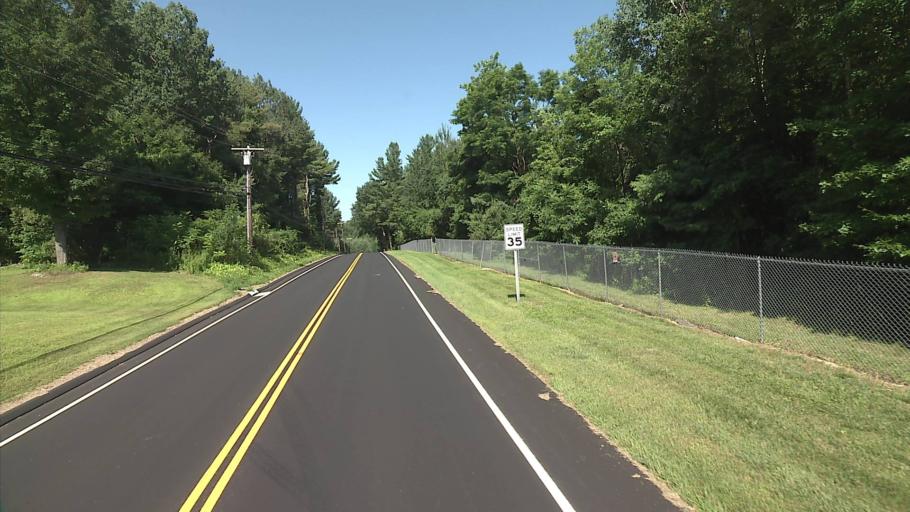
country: US
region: Connecticut
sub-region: Litchfield County
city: Winchester Center
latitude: 41.9168
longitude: -73.1014
